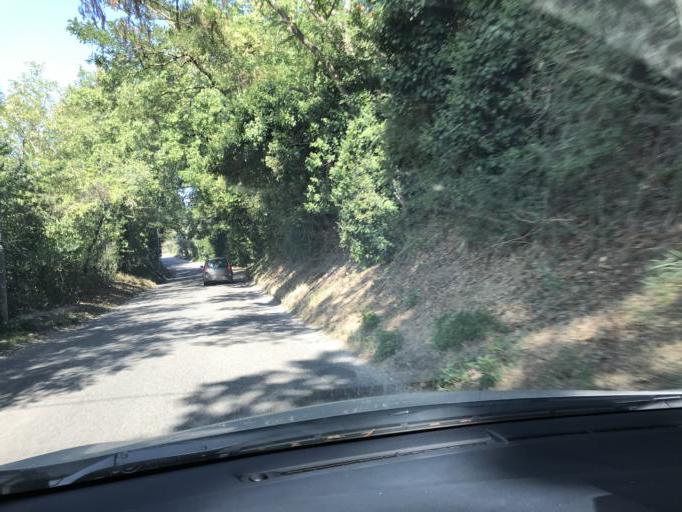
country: IT
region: Umbria
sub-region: Provincia di Perugia
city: Ponte Felcino
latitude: 43.1092
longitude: 12.4265
